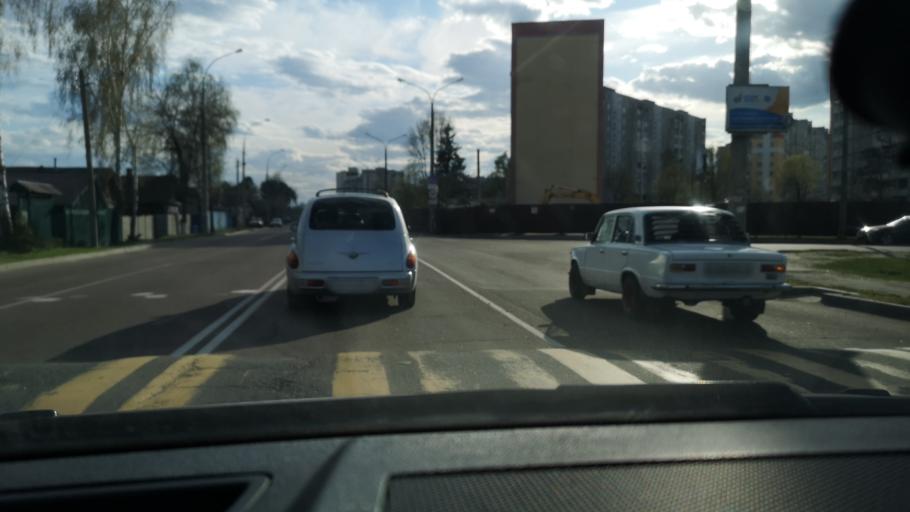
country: BY
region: Gomel
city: Gomel
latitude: 52.4036
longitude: 30.9321
